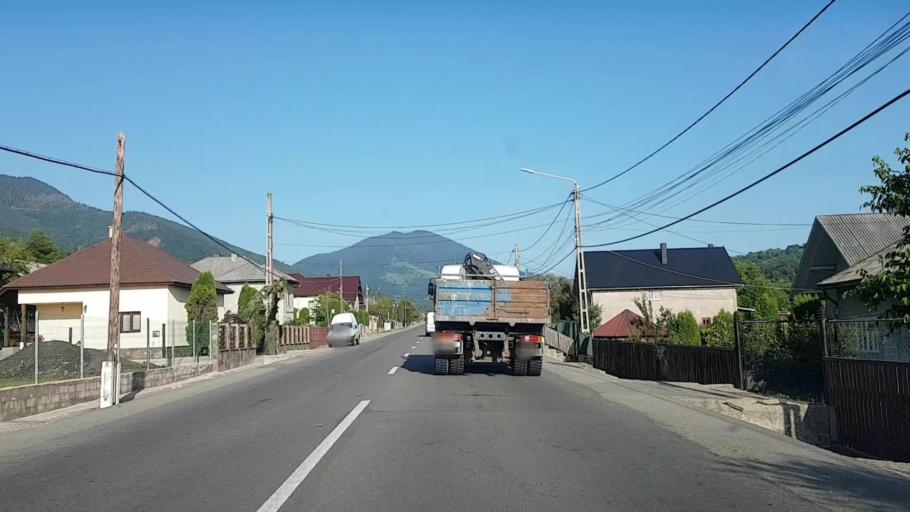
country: RO
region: Bistrita-Nasaud
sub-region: Comuna Tiha Bargaului
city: Tureac
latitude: 47.2269
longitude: 24.8091
